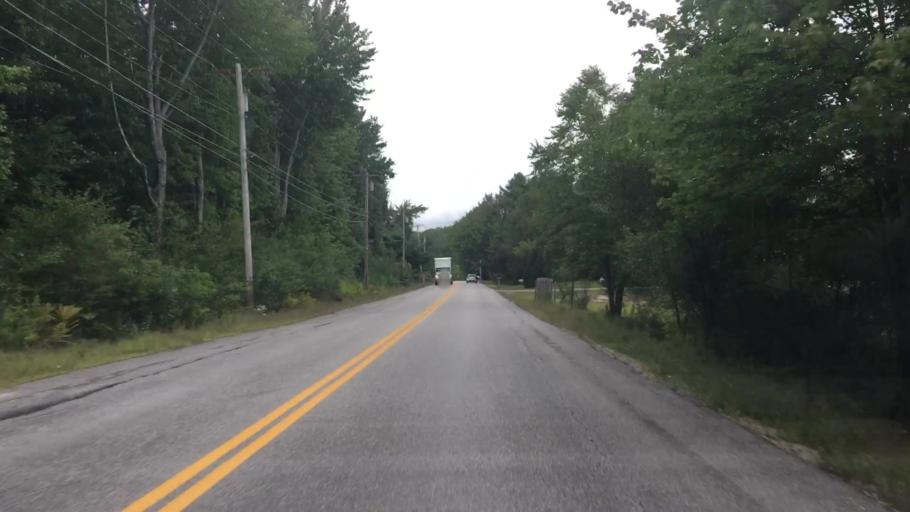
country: US
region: Maine
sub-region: Cumberland County
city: Yarmouth
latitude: 43.8345
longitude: -70.2031
